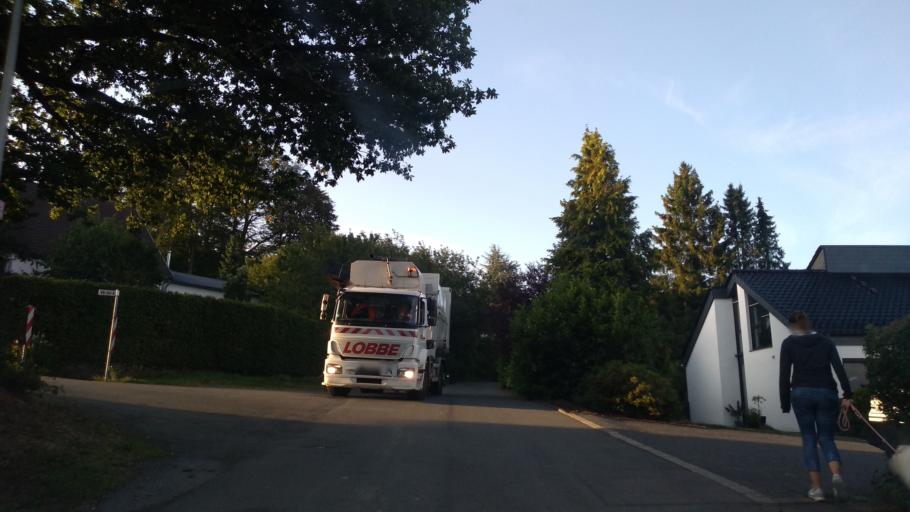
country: DE
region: North Rhine-Westphalia
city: Meinerzhagen
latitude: 51.0994
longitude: 7.6975
